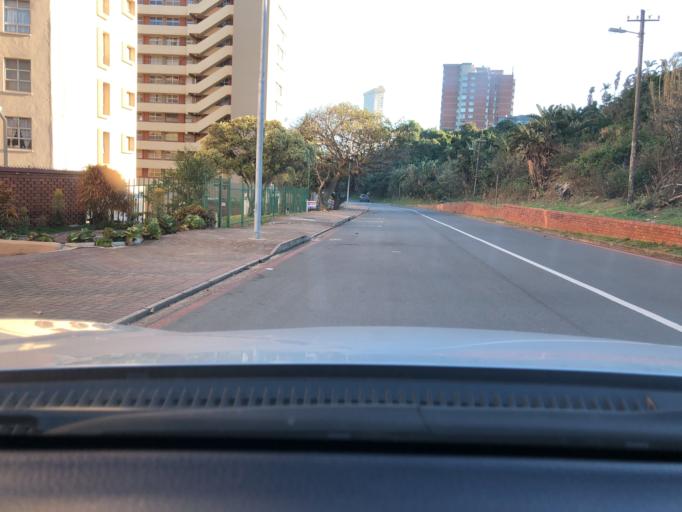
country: ZA
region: KwaZulu-Natal
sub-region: eThekwini Metropolitan Municipality
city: Umkomaas
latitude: -30.0454
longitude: 30.8924
